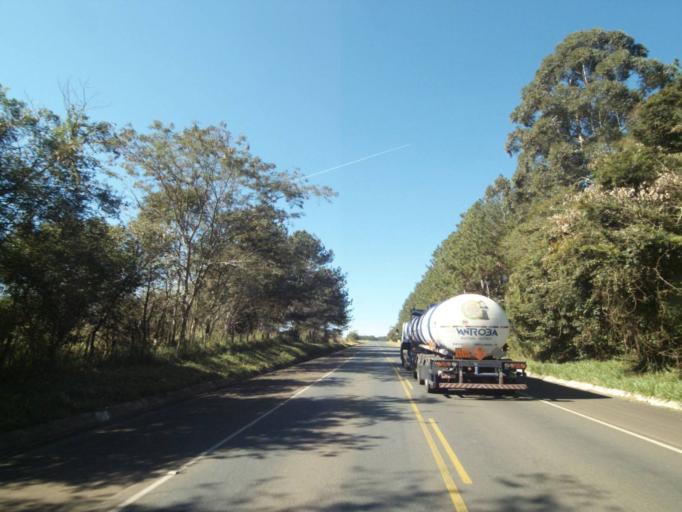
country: BR
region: Parana
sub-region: Tibagi
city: Tibagi
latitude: -24.4832
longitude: -50.4416
